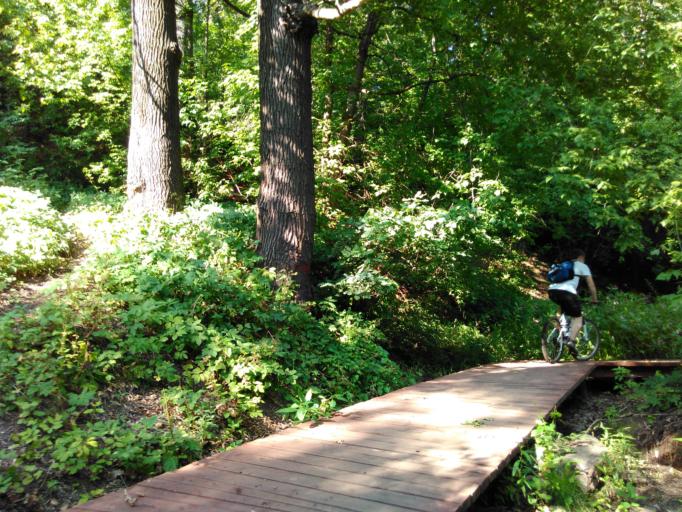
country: RU
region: Moscow
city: Amin'yevo
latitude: 55.7156
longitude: 37.4478
